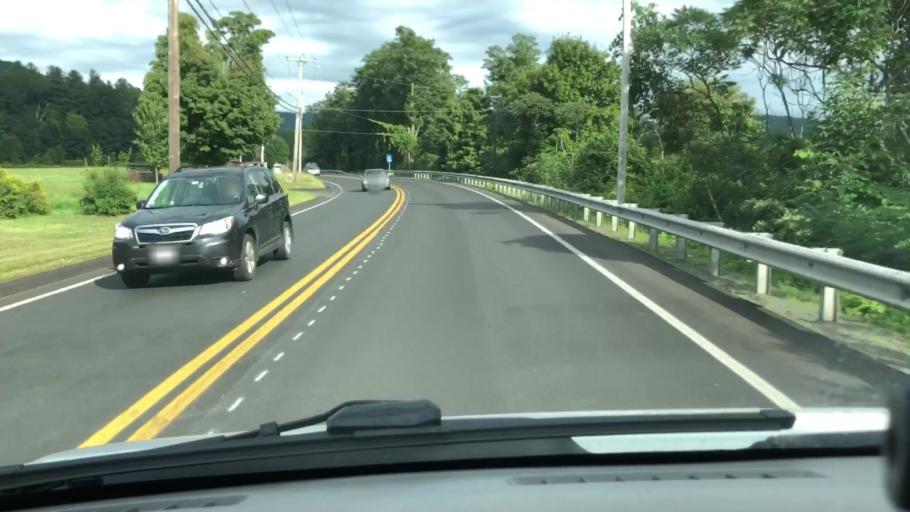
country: US
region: Massachusetts
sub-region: Franklin County
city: Buckland
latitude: 42.6211
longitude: -72.7749
